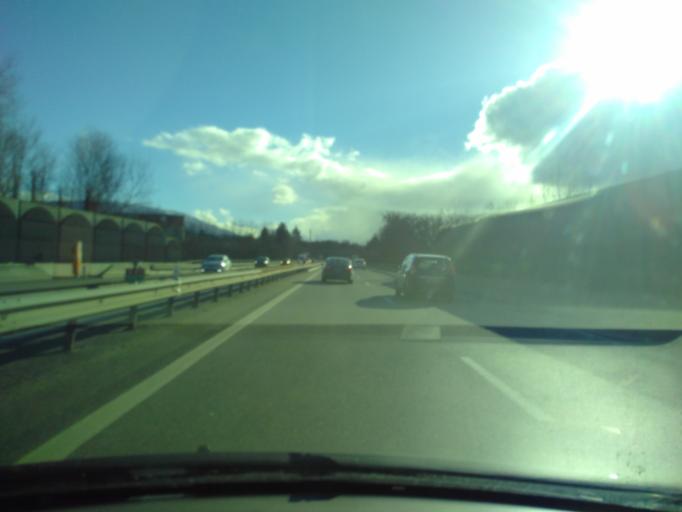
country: FR
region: Rhone-Alpes
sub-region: Departement de la Haute-Savoie
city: Meythet
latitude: 45.9089
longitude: 6.0953
